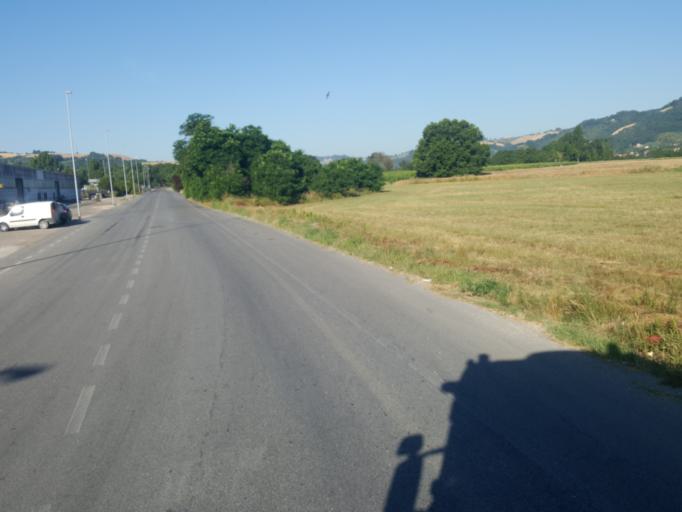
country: IT
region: The Marches
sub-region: Provincia di Pesaro e Urbino
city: Padiglione
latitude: 43.8393
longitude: 12.7221
